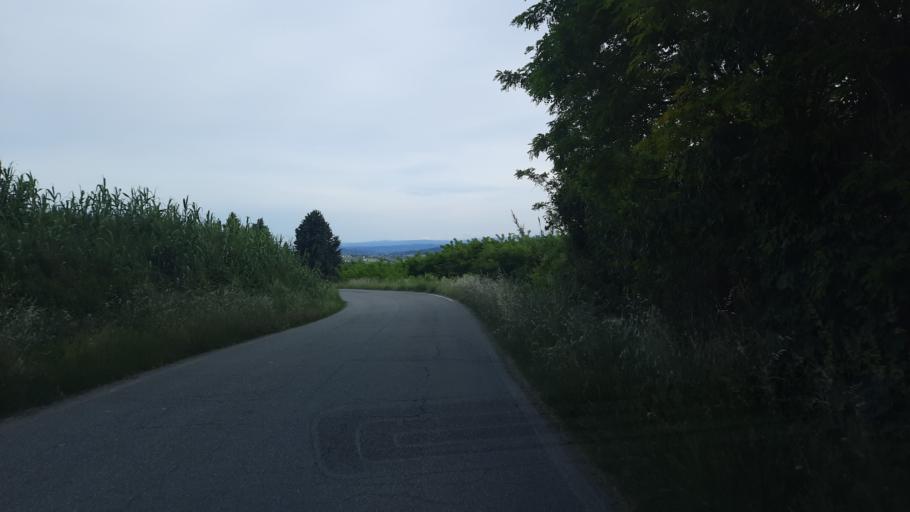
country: IT
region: Piedmont
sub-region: Provincia di Alessandria
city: Alfiano Natta
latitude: 45.0467
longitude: 8.2181
